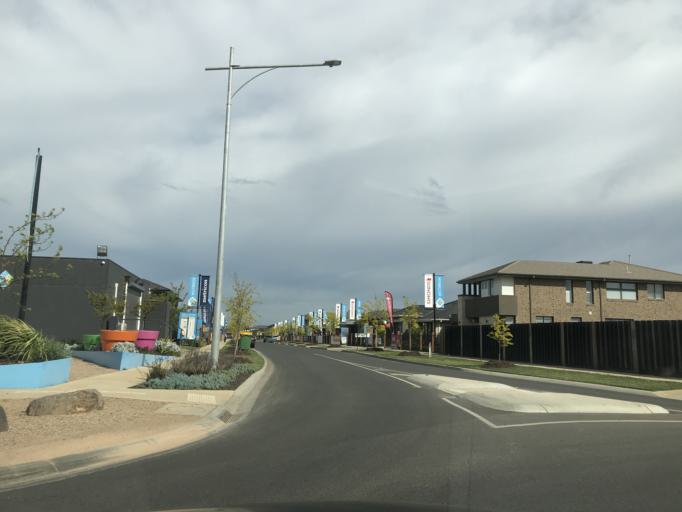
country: AU
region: Victoria
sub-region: Wyndham
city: Williams Landing
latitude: -37.8349
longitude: 144.7146
